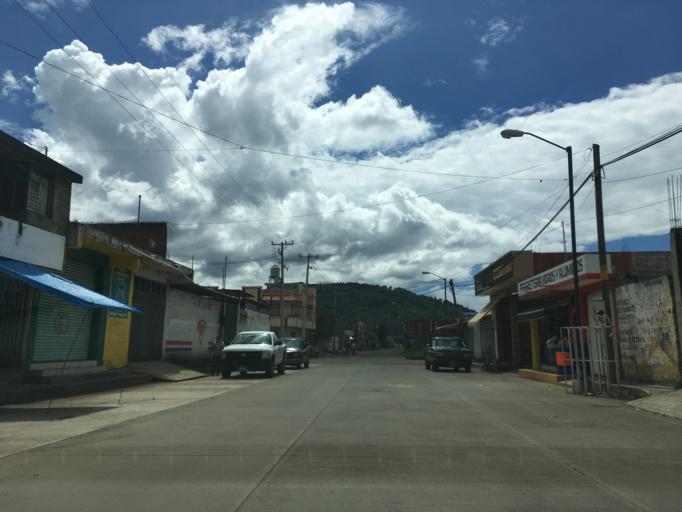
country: MX
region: Michoacan
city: Nahuatzen
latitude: 19.6541
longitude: -101.9199
